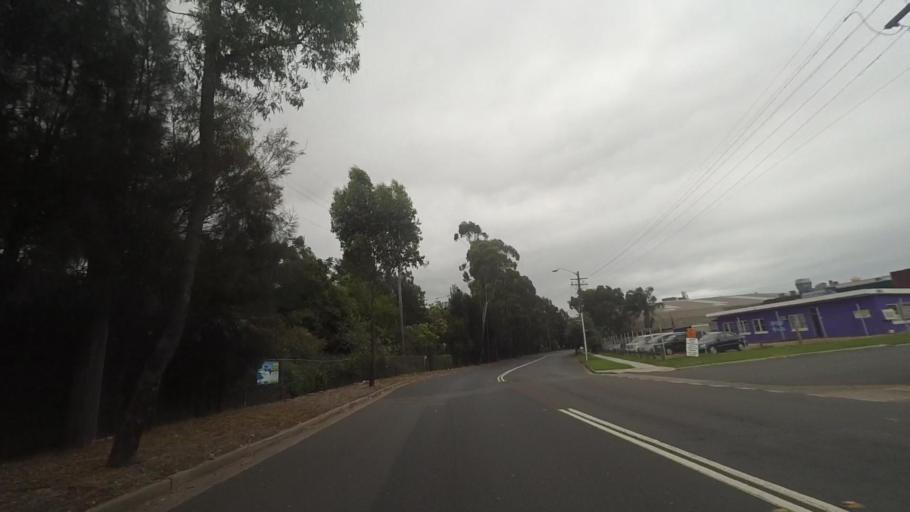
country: AU
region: New South Wales
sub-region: Auburn
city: Auburn
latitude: -33.8430
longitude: 151.0272
